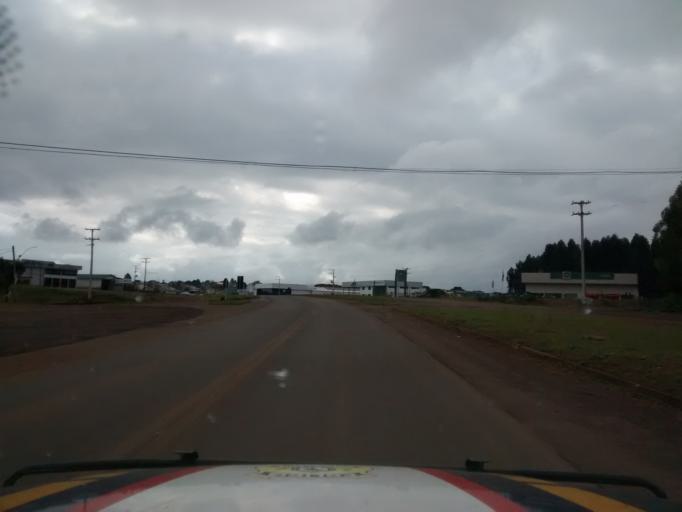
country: BR
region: Rio Grande do Sul
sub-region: Lagoa Vermelha
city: Lagoa Vermelha
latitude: -28.2117
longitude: -51.5107
